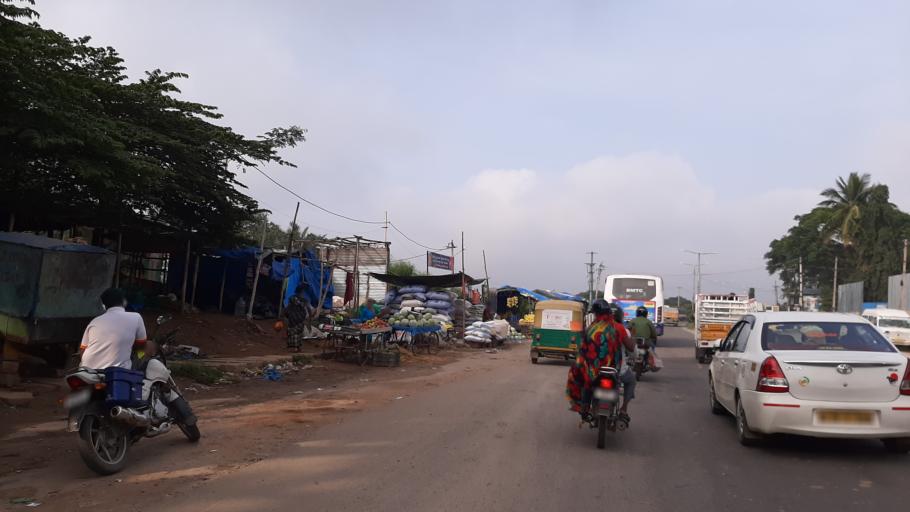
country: IN
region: Karnataka
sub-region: Bangalore Urban
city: Bangalore
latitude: 12.9894
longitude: 77.5011
